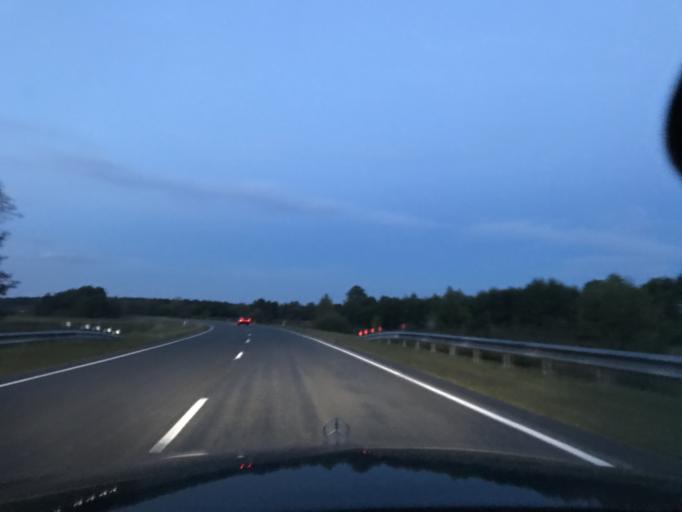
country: PL
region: Lublin Voivodeship
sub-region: Powiat bialski
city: Slawatycze
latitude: 51.7602
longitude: 23.6329
